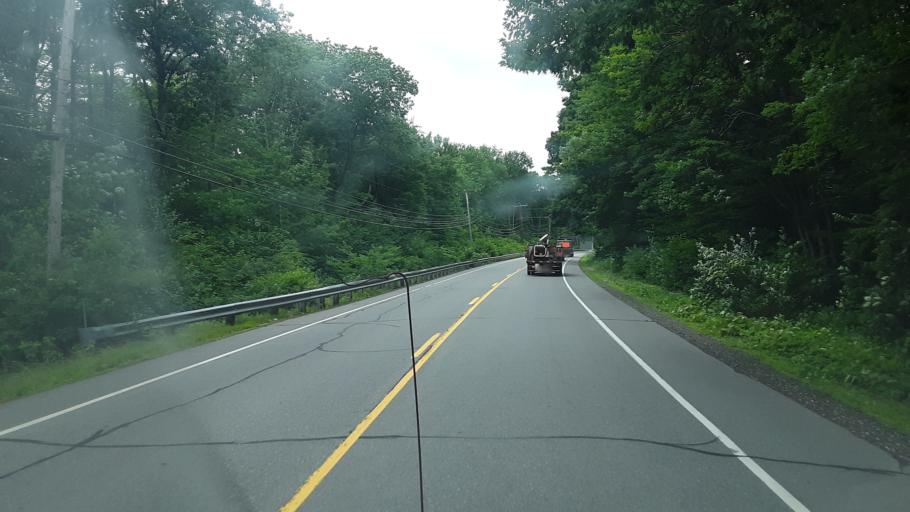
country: US
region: New Hampshire
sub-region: Rockingham County
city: Northwood
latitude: 43.1821
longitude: -71.1225
